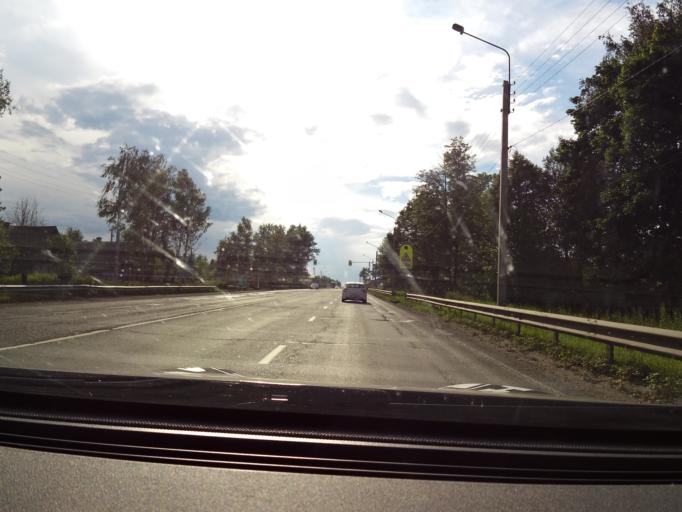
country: RU
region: Vladimir
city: Gorokhovets
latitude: 56.1690
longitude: 42.4468
